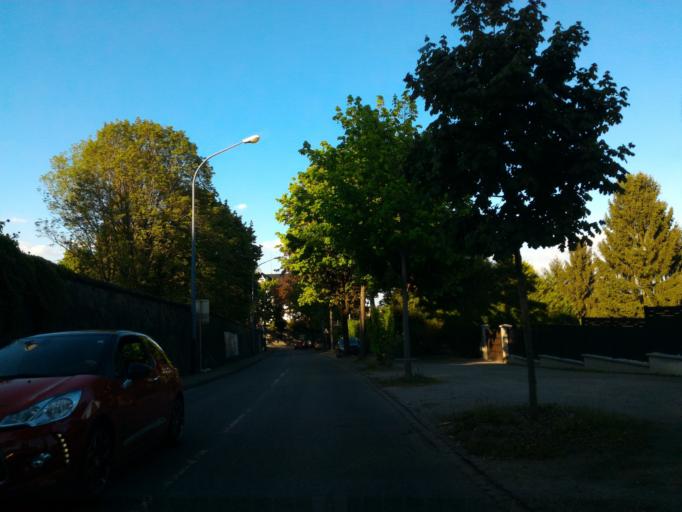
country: FR
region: Alsace
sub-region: Departement du Haut-Rhin
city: Riedisheim
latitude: 47.7389
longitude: 7.3525
